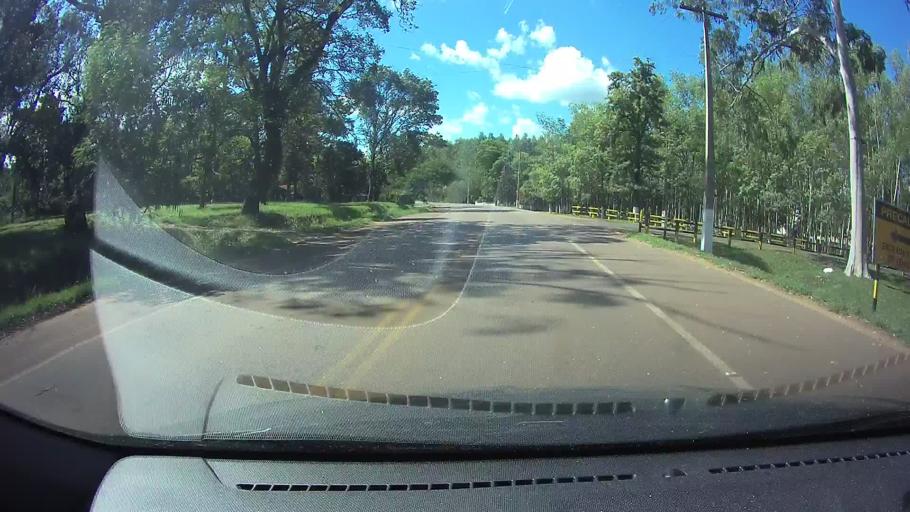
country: PY
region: Guaira
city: Coronel Martinez
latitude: -25.7710
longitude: -56.6519
